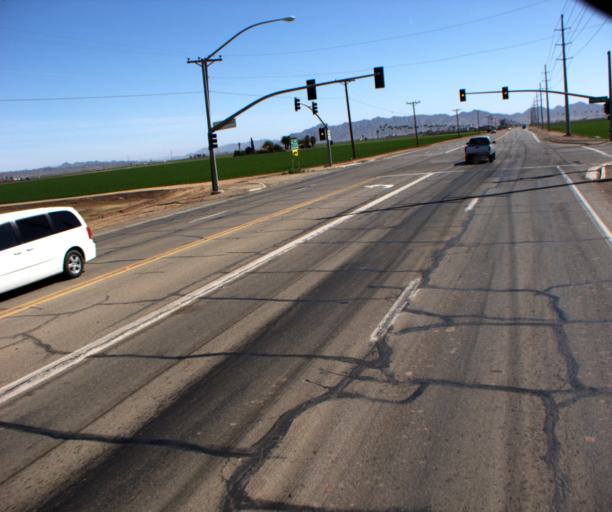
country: US
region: Arizona
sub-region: Yuma County
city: Yuma
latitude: 32.6991
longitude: -114.5221
